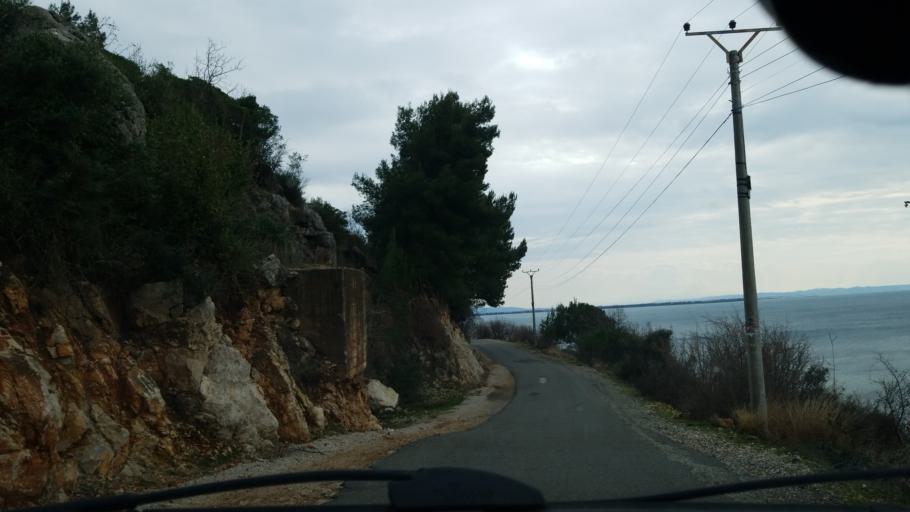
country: AL
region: Lezhe
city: Shengjin
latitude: 41.8163
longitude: 19.5685
